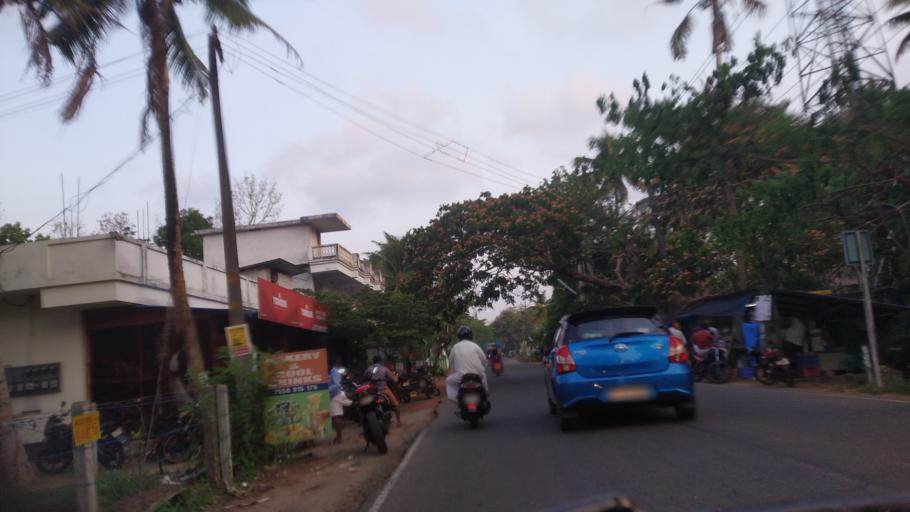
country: IN
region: Kerala
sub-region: Thrissur District
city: Kodungallur
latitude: 10.2215
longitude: 76.1583
